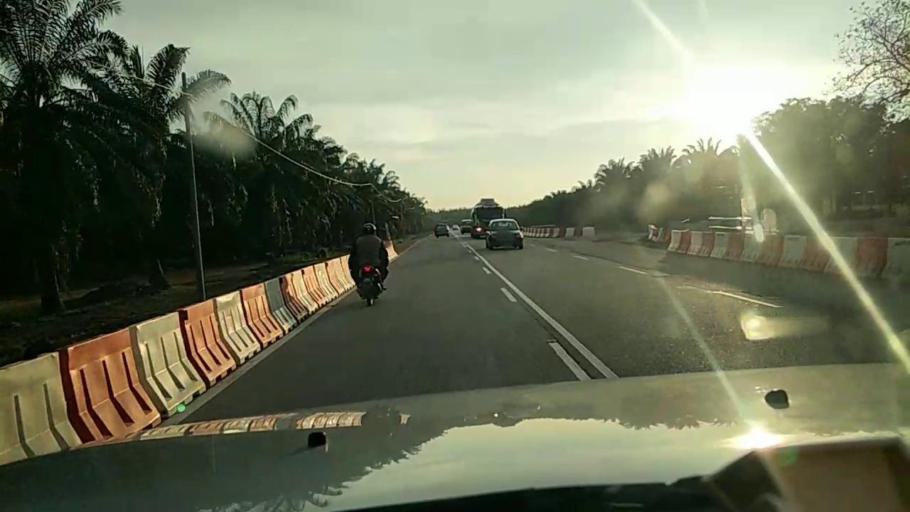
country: MY
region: Selangor
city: Batang Berjuntai
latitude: 3.3057
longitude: 101.3590
